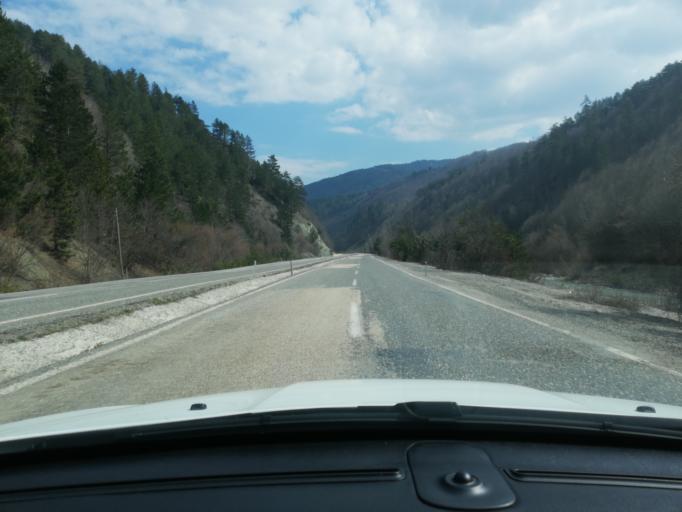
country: TR
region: Kastamonu
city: Kuzyaka
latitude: 41.1298
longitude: 33.7695
